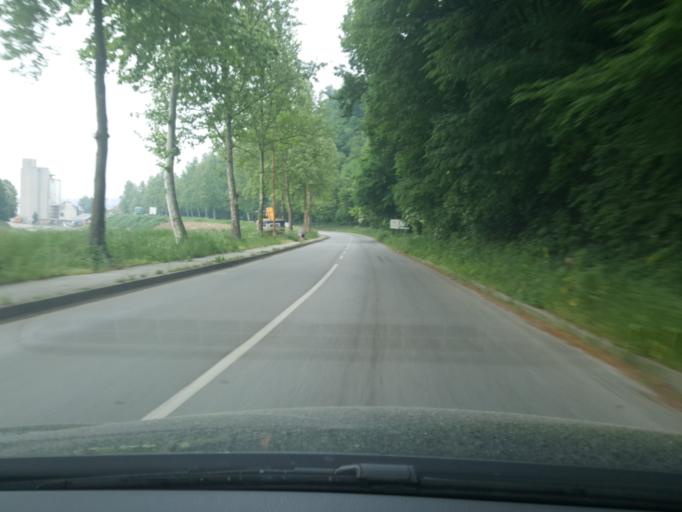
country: RS
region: Central Serbia
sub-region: Kolubarski Okrug
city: Valjevo
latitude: 44.2620
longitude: 19.8769
